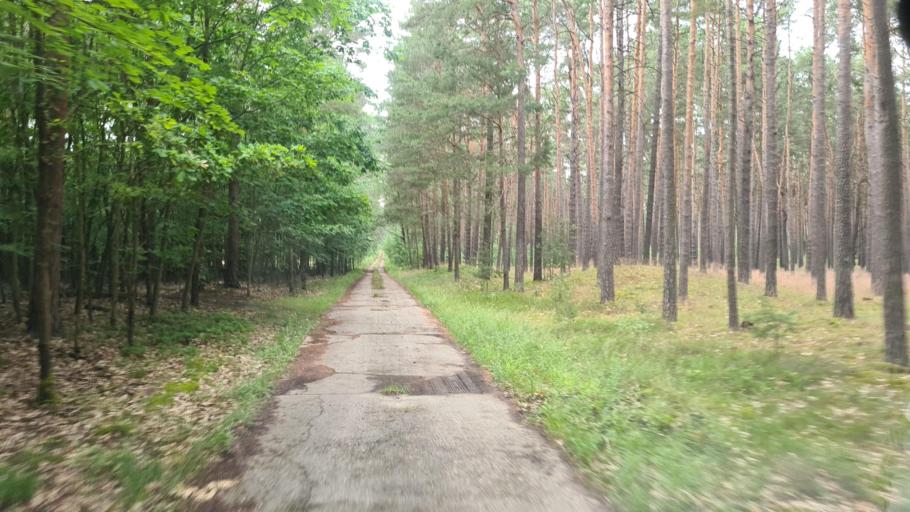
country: DE
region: Brandenburg
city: Crinitz
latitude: 51.7180
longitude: 13.7142
